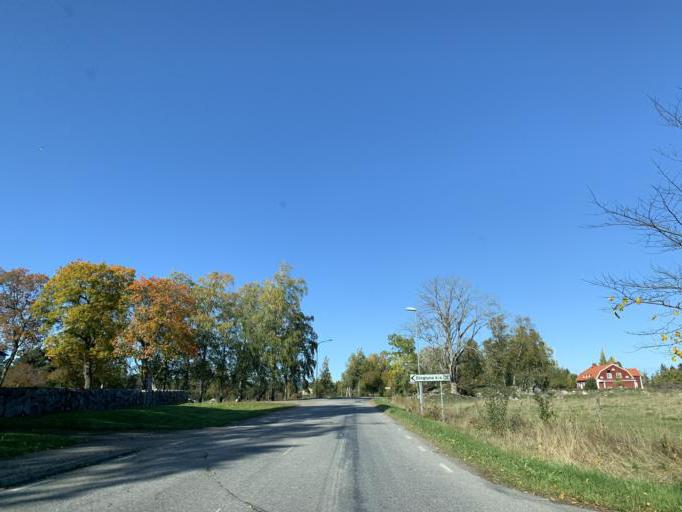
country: SE
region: Soedermanland
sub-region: Eskilstuna Kommun
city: Kvicksund
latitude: 59.5694
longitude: 16.4030
